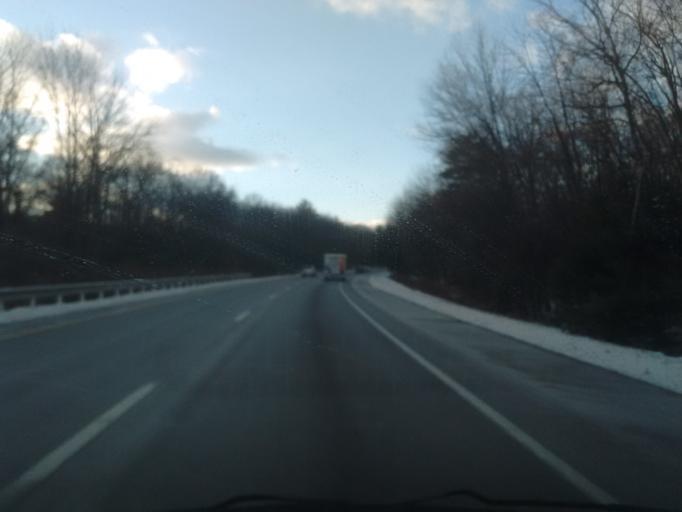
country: US
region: Pennsylvania
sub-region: Pike County
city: Milford
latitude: 41.3330
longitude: -74.8528
